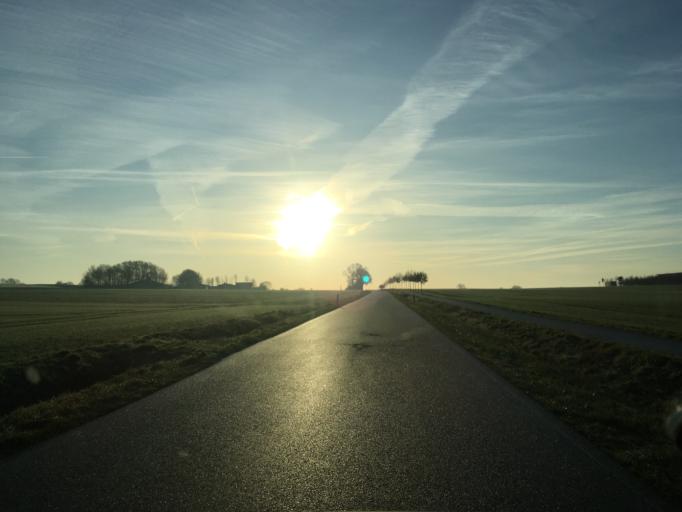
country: DE
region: North Rhine-Westphalia
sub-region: Regierungsbezirk Munster
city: Schoppingen
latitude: 52.0855
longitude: 7.2468
